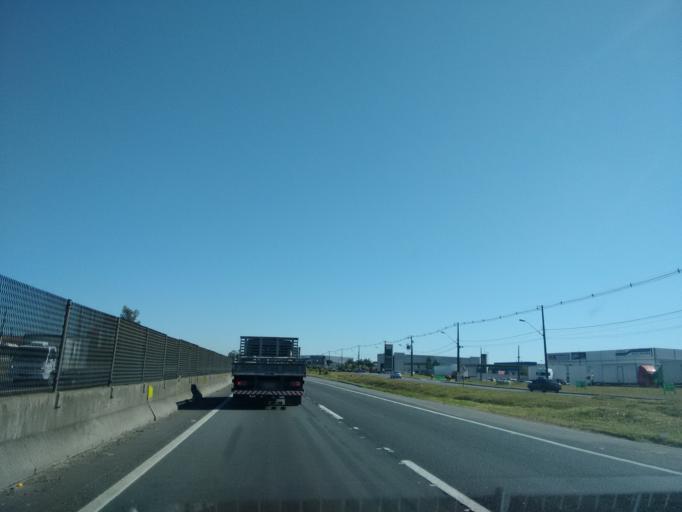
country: BR
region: Parana
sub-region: Sao Jose Dos Pinhais
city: Sao Jose dos Pinhais
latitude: -25.5494
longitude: -49.2835
